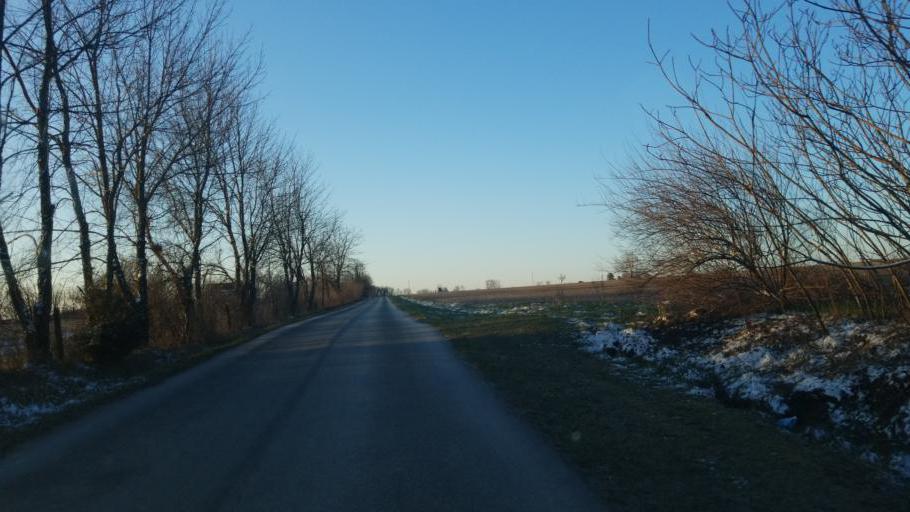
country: US
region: Ohio
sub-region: Highland County
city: Leesburg
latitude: 39.2767
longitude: -83.5017
